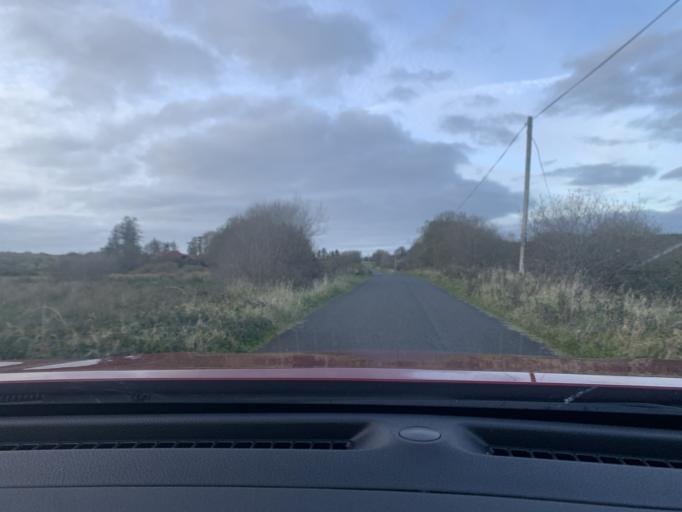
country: IE
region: Connaught
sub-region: Roscommon
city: Ballaghaderreen
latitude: 53.9322
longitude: -8.5896
